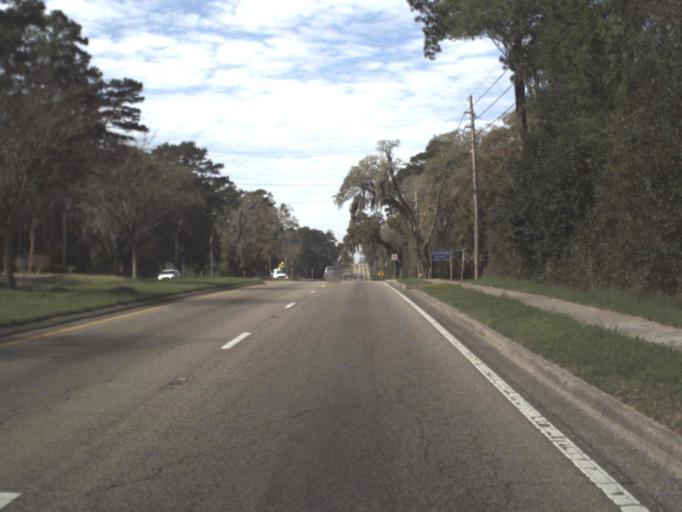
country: US
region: Florida
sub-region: Leon County
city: Tallahassee
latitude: 30.4543
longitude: -84.2443
